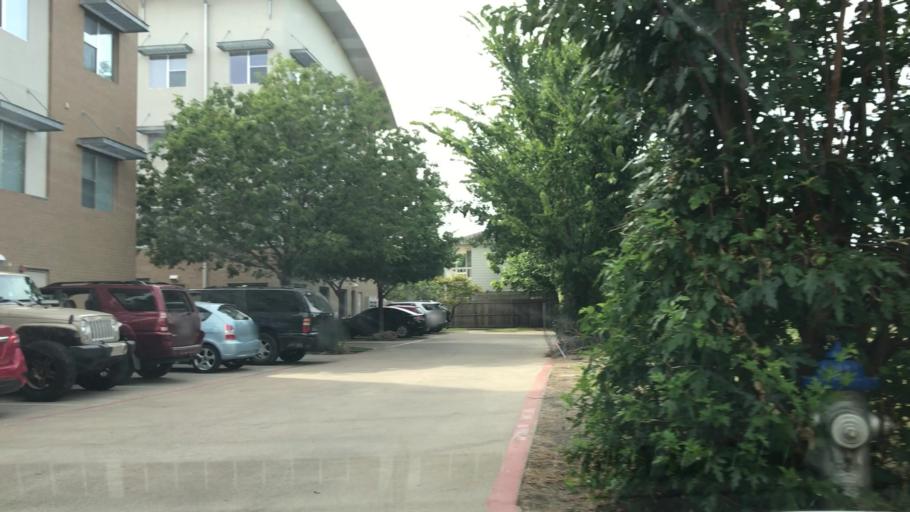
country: US
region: Texas
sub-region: Dallas County
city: Dallas
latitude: 32.7920
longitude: -96.7877
